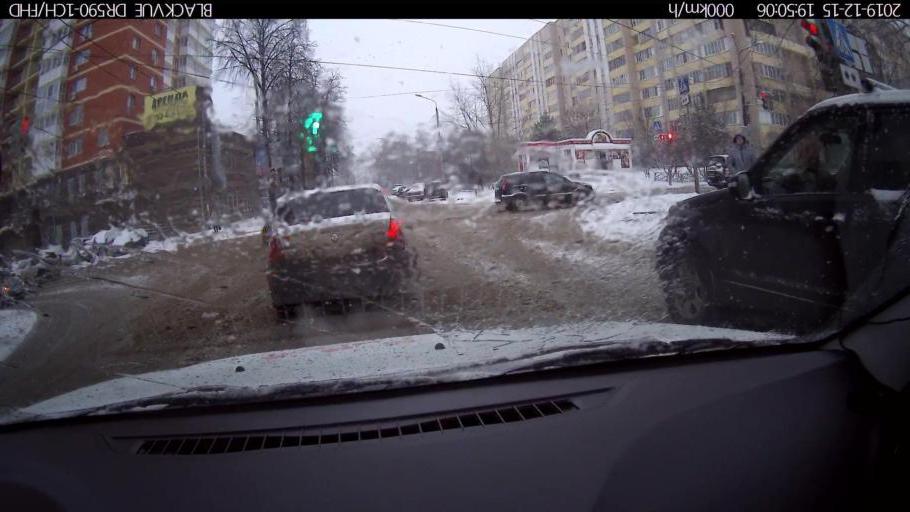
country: RU
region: Nizjnij Novgorod
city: Nizhniy Novgorod
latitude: 56.3128
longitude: 44.0282
